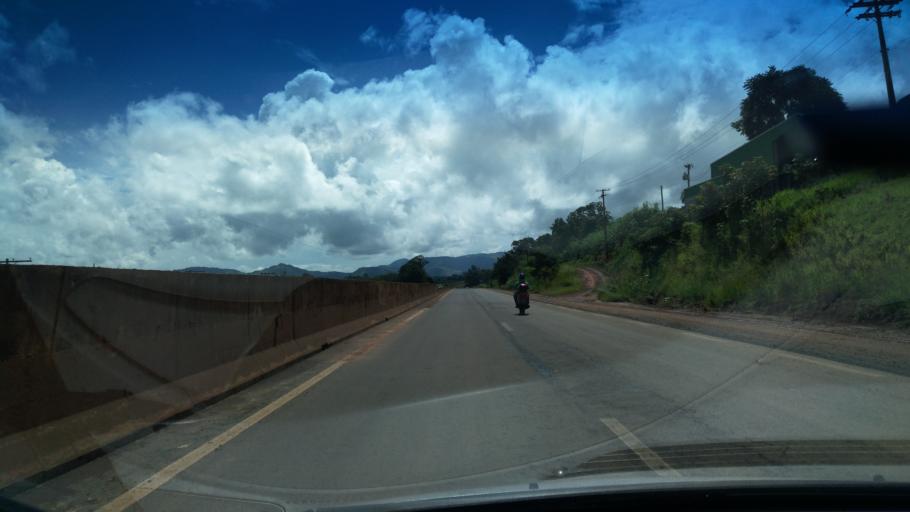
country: BR
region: Sao Paulo
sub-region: Santo Antonio Do Jardim
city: Espirito Santo do Pinhal
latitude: -22.1170
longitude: -46.6797
